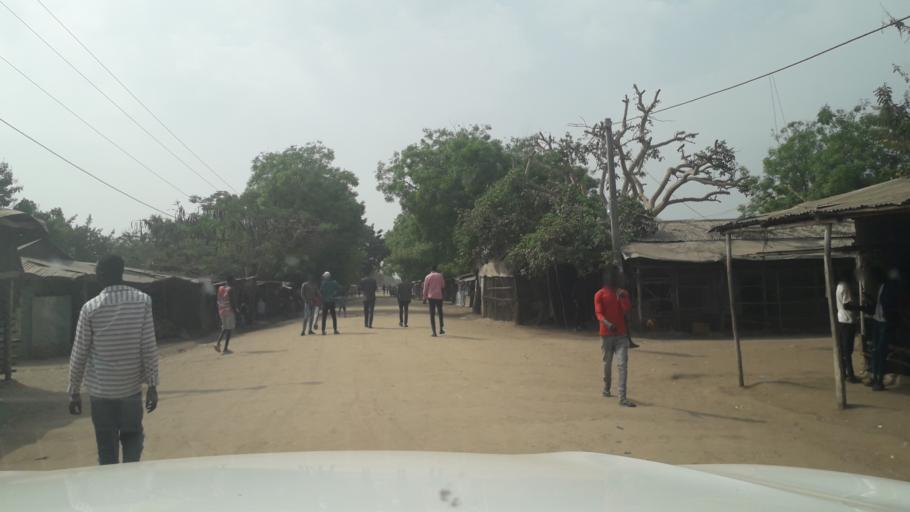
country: ET
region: Gambela
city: Gambela
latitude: 8.3008
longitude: 33.6830
